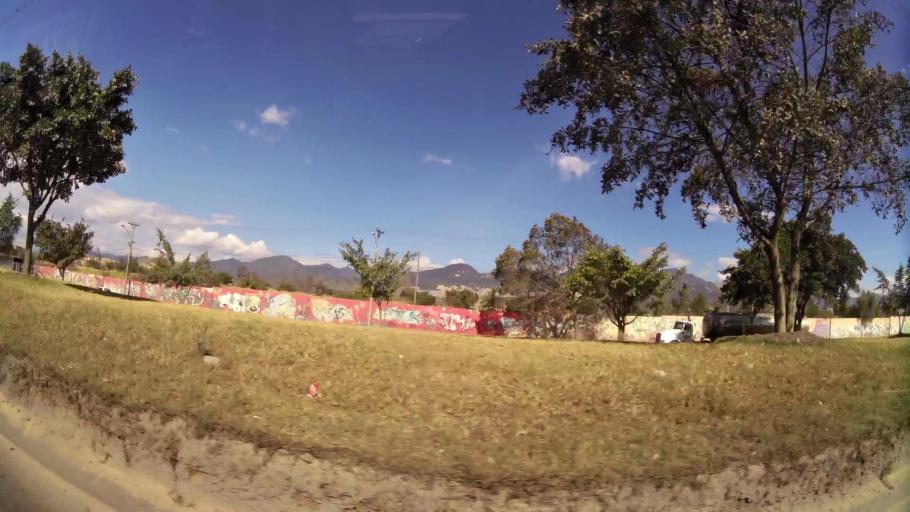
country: CO
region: Bogota D.C.
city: Bogota
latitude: 4.5504
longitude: -74.1366
